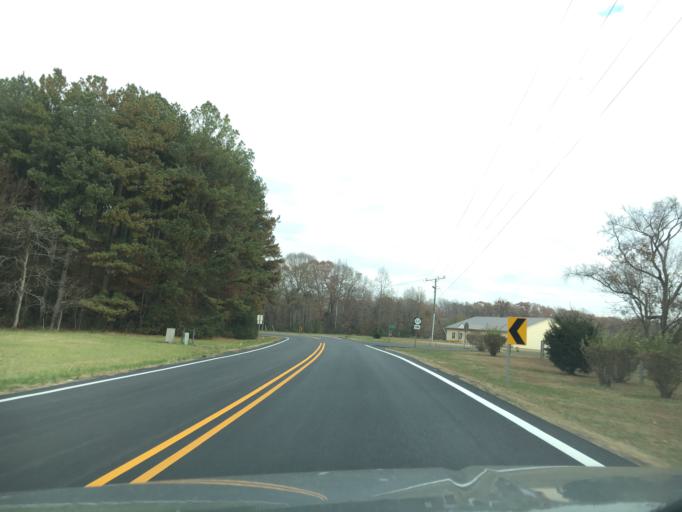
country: US
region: Virginia
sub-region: Cumberland County
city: Cumberland
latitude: 37.4611
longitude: -78.2836
